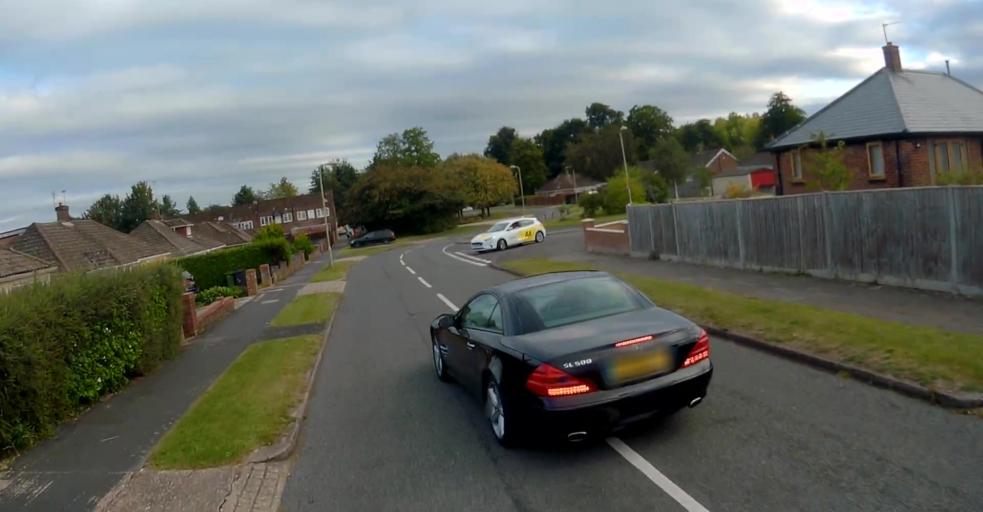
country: GB
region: England
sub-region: Hampshire
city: Basingstoke
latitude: 51.2512
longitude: -1.1192
